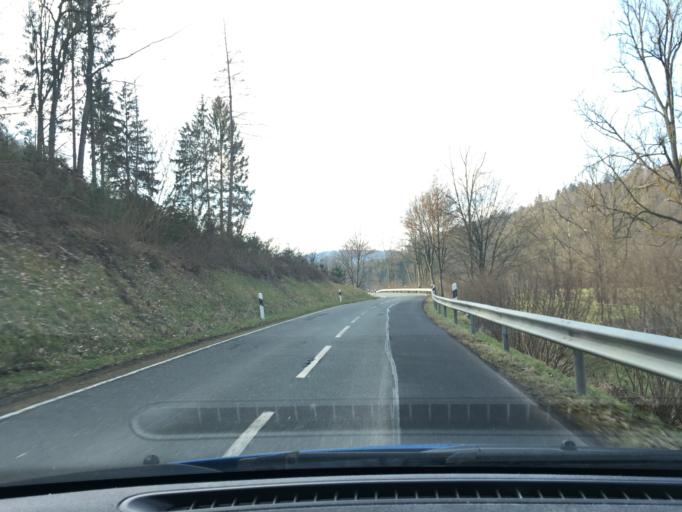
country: DE
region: Lower Saxony
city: Uslar
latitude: 51.6205
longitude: 9.6462
